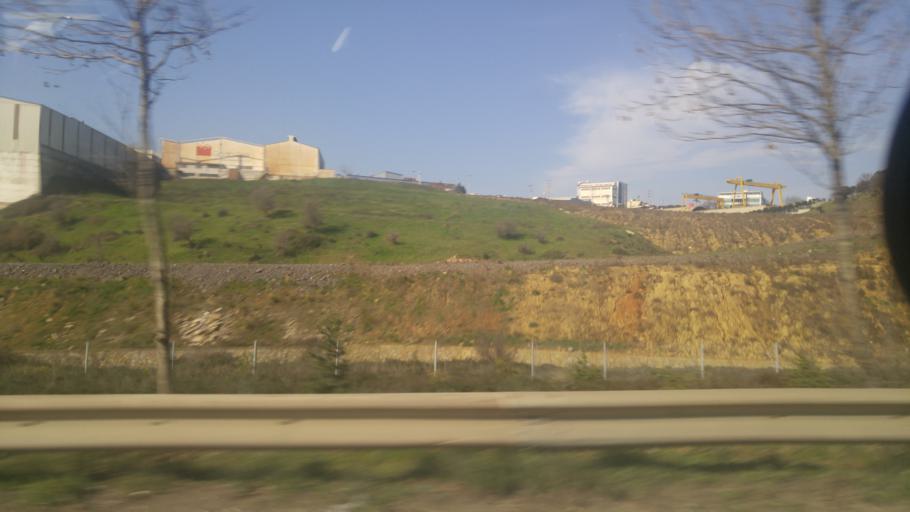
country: TR
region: Kocaeli
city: Balcik
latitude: 40.8445
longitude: 29.3743
